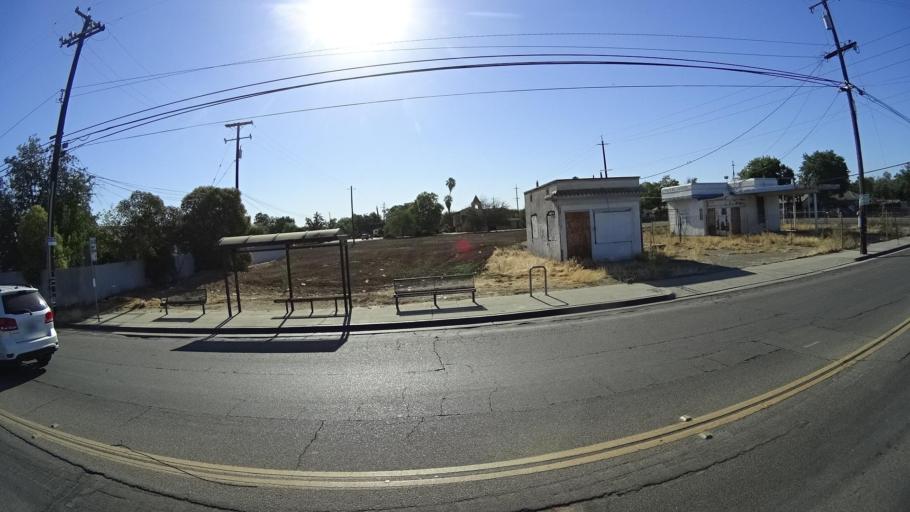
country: US
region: California
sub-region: Fresno County
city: Fresno
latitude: 36.7073
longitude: -119.7999
